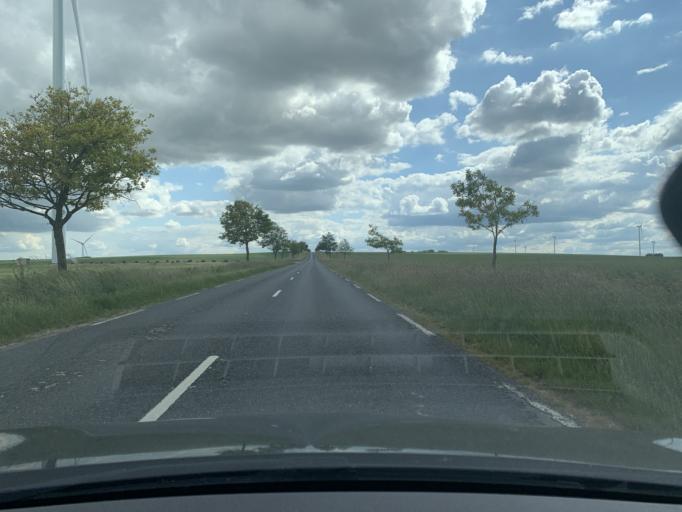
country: FR
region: Picardie
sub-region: Departement de la Somme
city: Moislains
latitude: 50.0212
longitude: 3.0335
